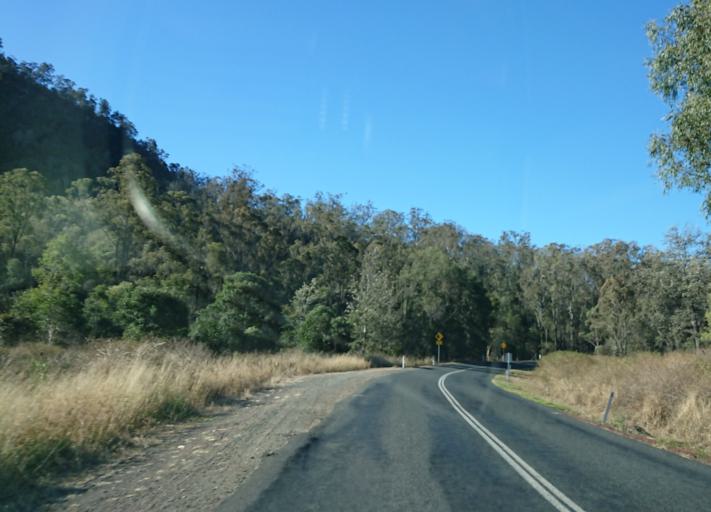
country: AU
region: Queensland
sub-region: Toowoomba
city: Top Camp
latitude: -27.7383
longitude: 152.0996
